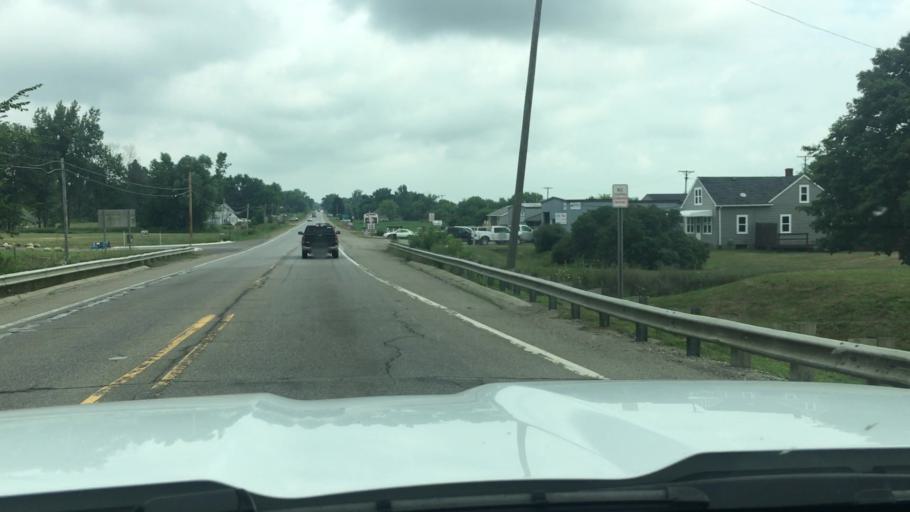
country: US
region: Michigan
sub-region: Lapeer County
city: Imlay City
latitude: 43.0326
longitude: -83.0716
